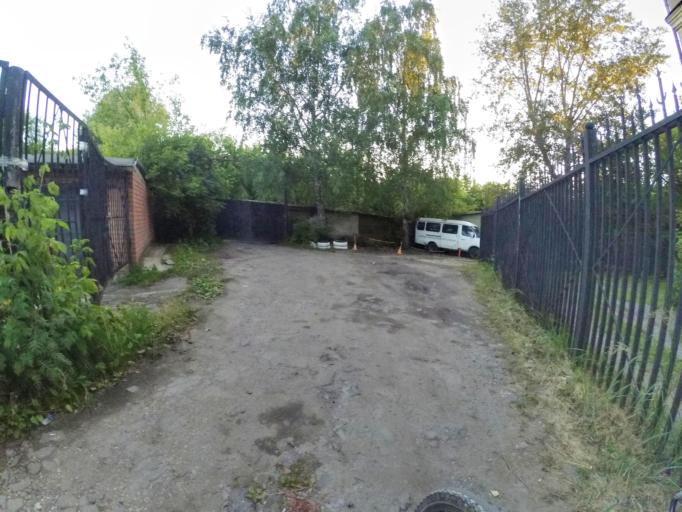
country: RU
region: Moscow
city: Pokrovskoye-Streshnevo
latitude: 55.8160
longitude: 37.4479
